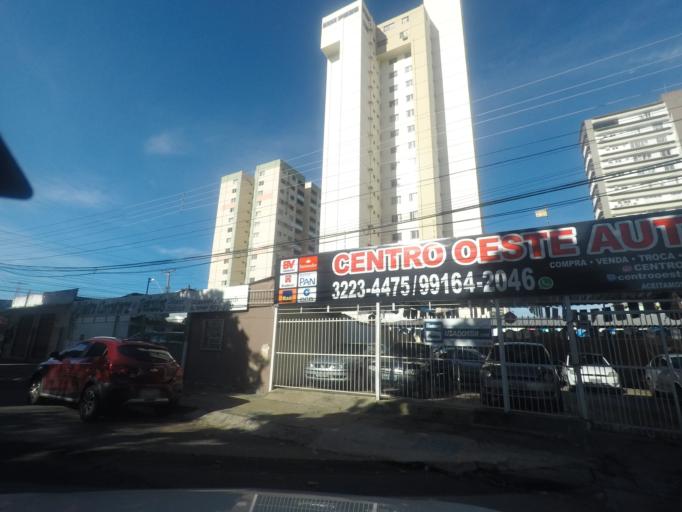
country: BR
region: Goias
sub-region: Goiania
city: Goiania
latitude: -16.6689
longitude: -49.2690
